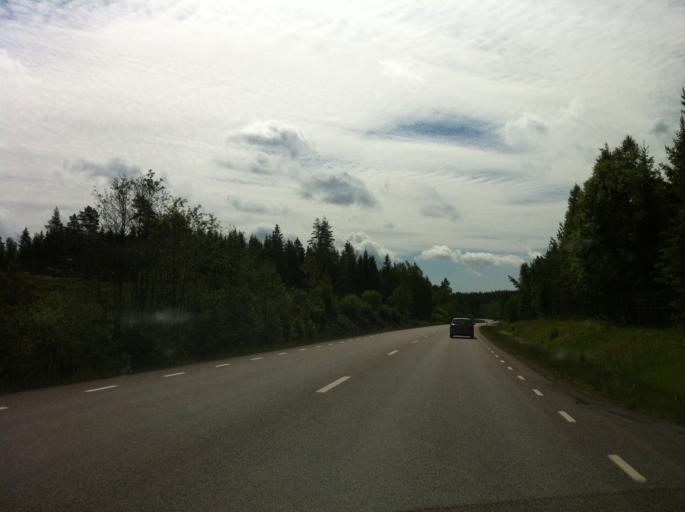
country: SE
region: Vaermland
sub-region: Saffle Kommun
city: Saeffle
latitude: 59.2268
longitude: 13.0051
